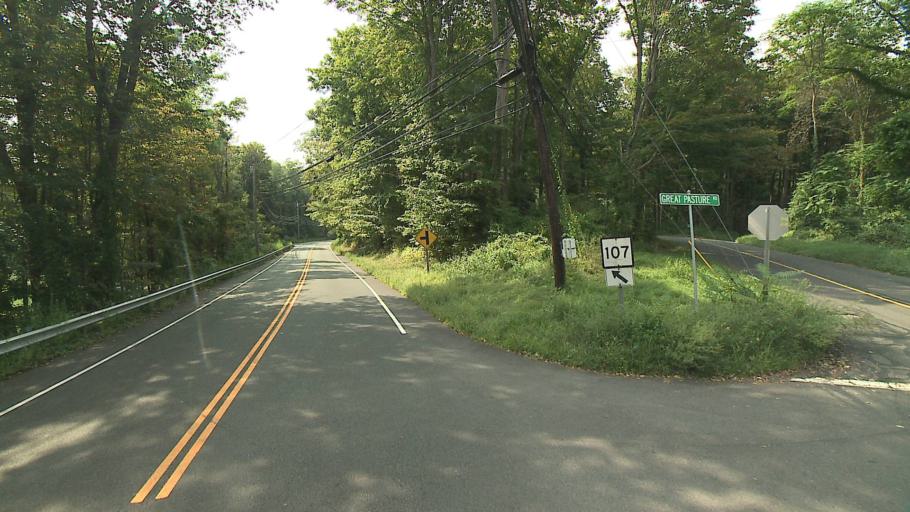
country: US
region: Connecticut
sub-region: Fairfield County
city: Georgetown
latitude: 41.3006
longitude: -73.3881
